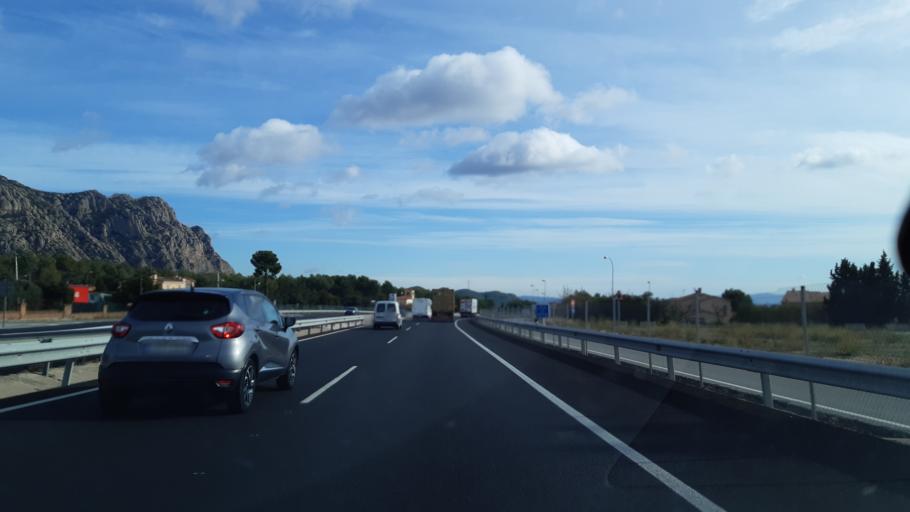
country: ES
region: Catalonia
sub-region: Provincia de Barcelona
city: Collbato
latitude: 41.5687
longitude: 1.8017
